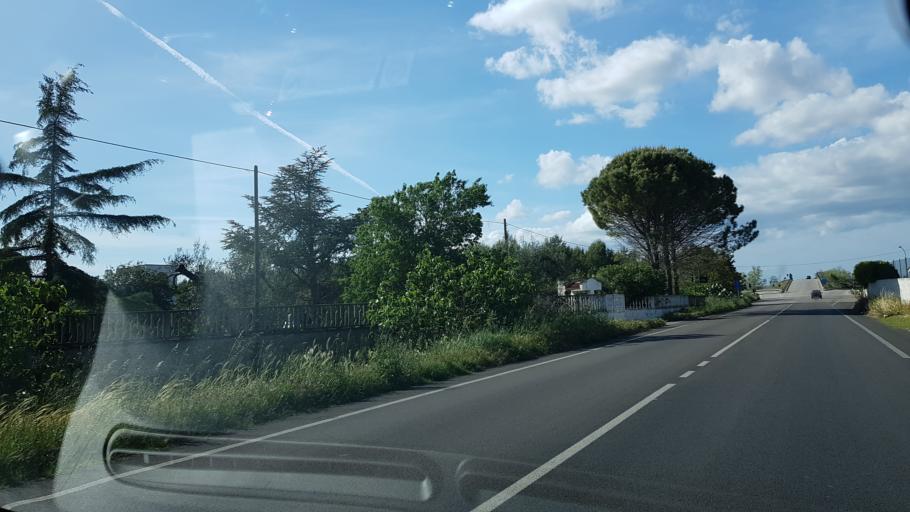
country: IT
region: Apulia
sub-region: Provincia di Brindisi
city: Mesagne
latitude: 40.5646
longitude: 17.7869
